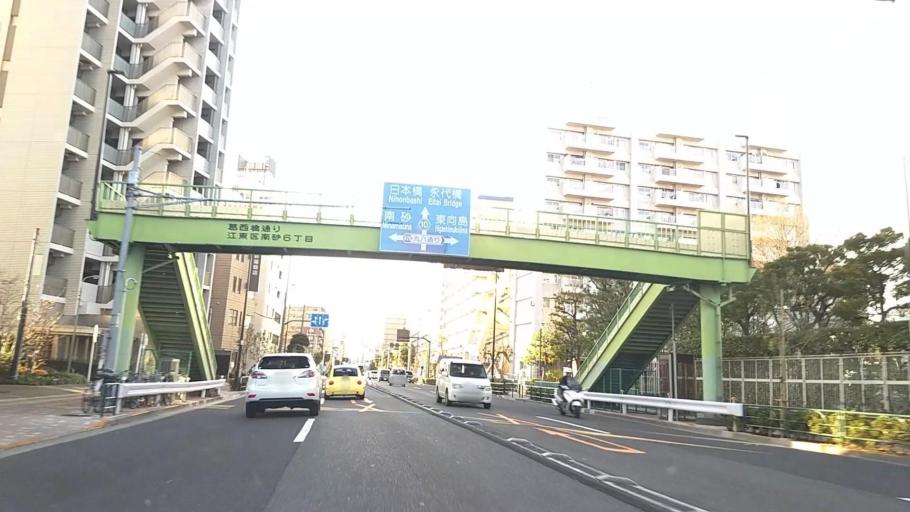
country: JP
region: Tokyo
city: Urayasu
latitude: 35.6729
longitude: 139.8347
